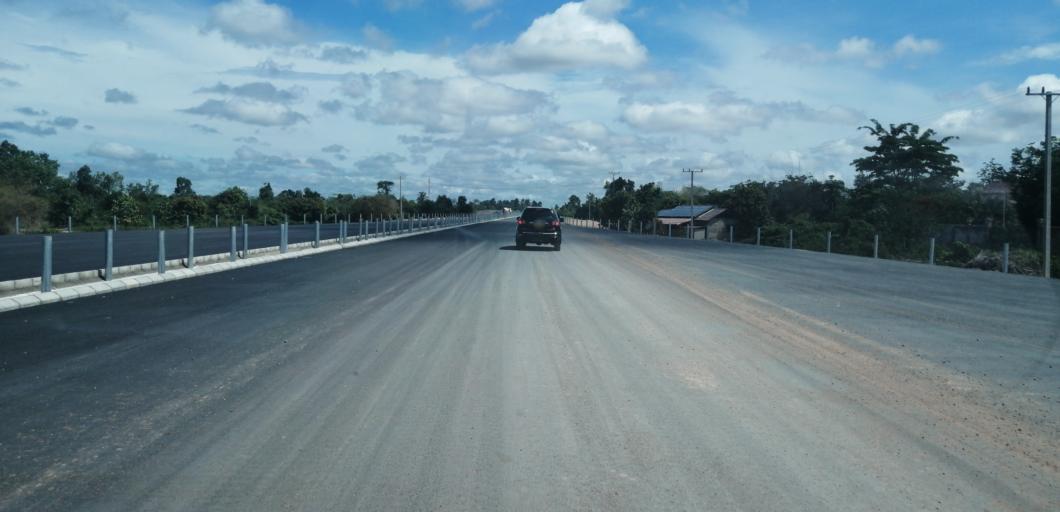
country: LA
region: Vientiane
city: Vientiane
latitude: 18.0510
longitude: 102.5251
